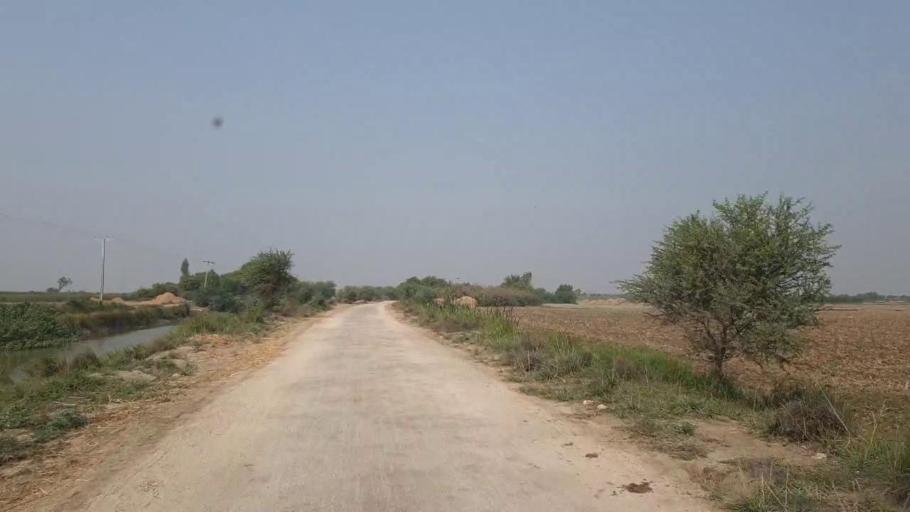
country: PK
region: Sindh
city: Kario
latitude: 24.9143
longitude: 68.6026
